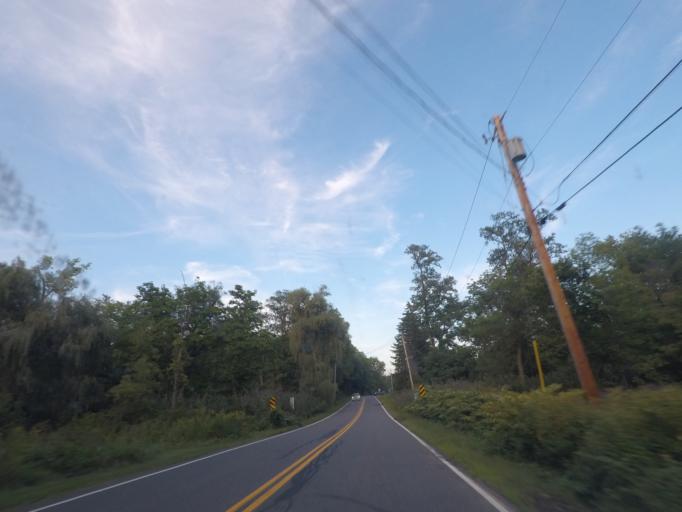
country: US
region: New York
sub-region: Schenectady County
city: Niskayuna
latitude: 42.7706
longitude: -73.8087
